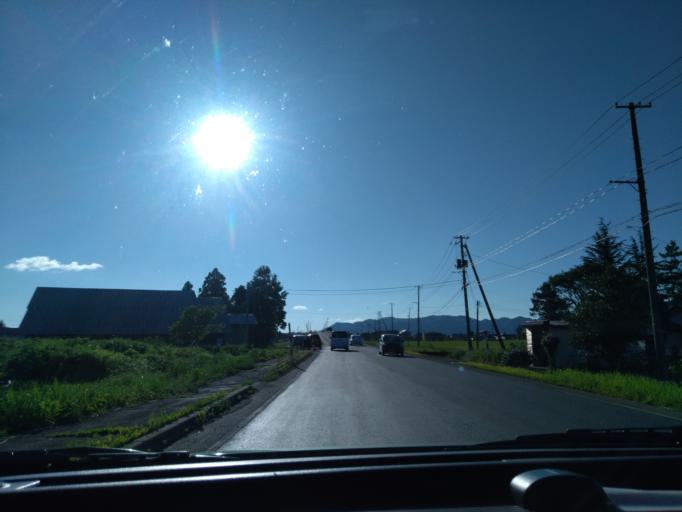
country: JP
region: Akita
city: Omagari
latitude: 39.4225
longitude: 140.5104
